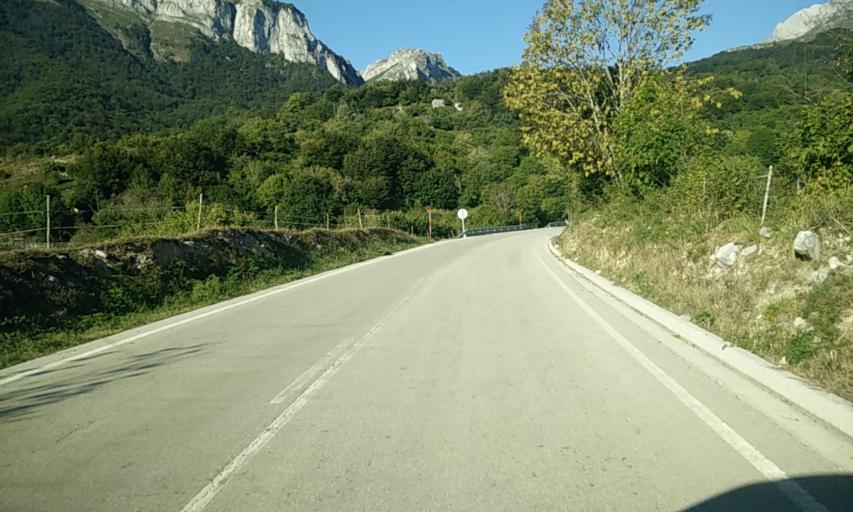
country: ES
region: Cantabria
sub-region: Provincia de Cantabria
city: Camaleno
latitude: 43.1305
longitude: -4.8044
